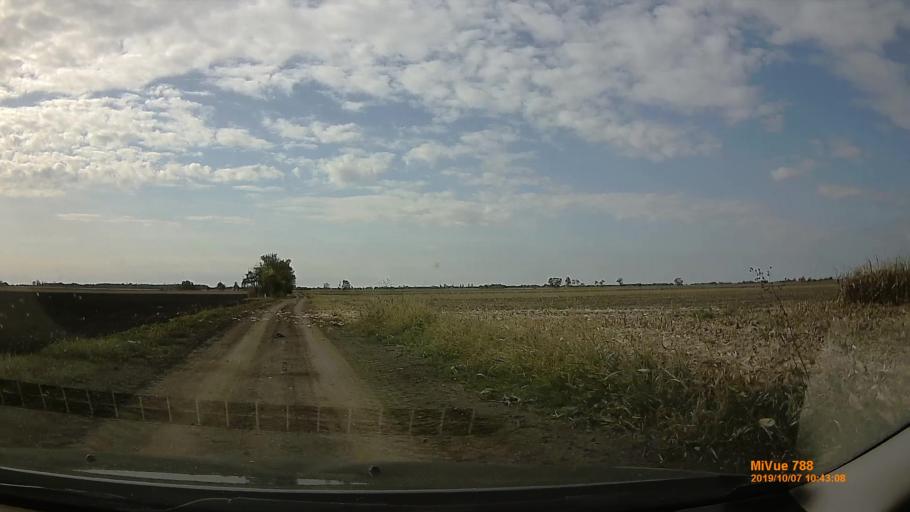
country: HU
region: Bekes
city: Kondoros
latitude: 46.7392
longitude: 20.8374
